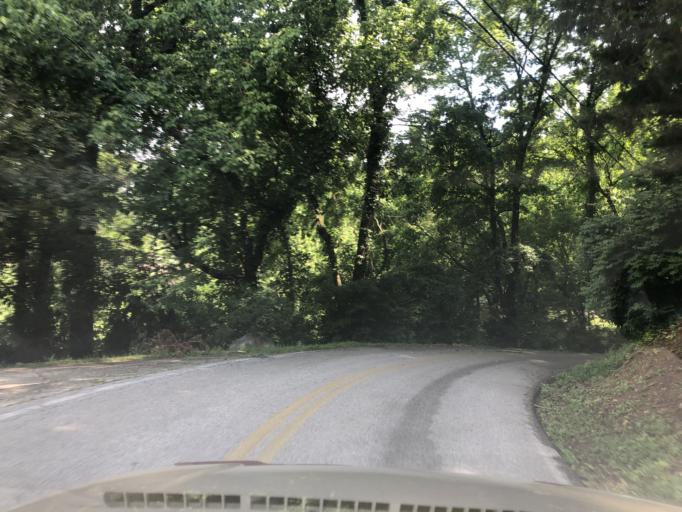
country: US
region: Tennessee
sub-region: Wilson County
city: Green Hill
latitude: 36.2435
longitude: -86.5889
